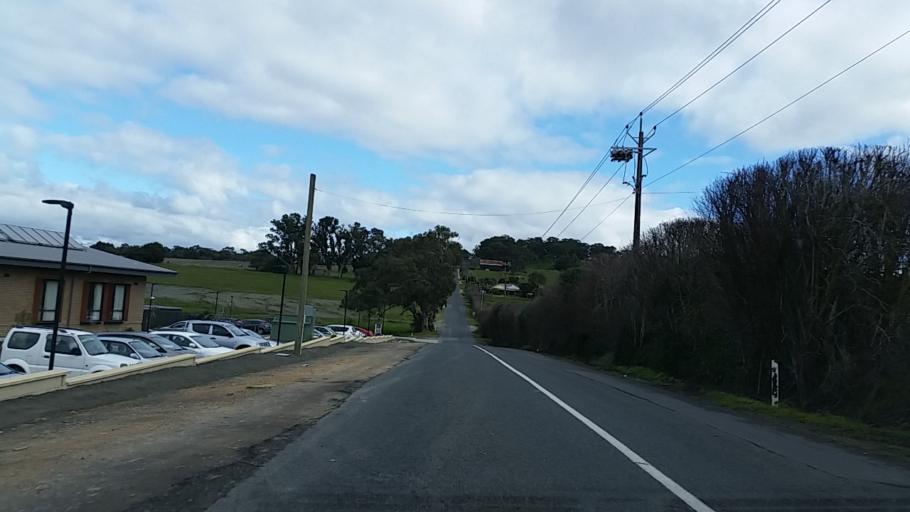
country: AU
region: South Australia
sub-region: Mount Barker
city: Little Hampton
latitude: -35.0653
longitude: 138.8507
